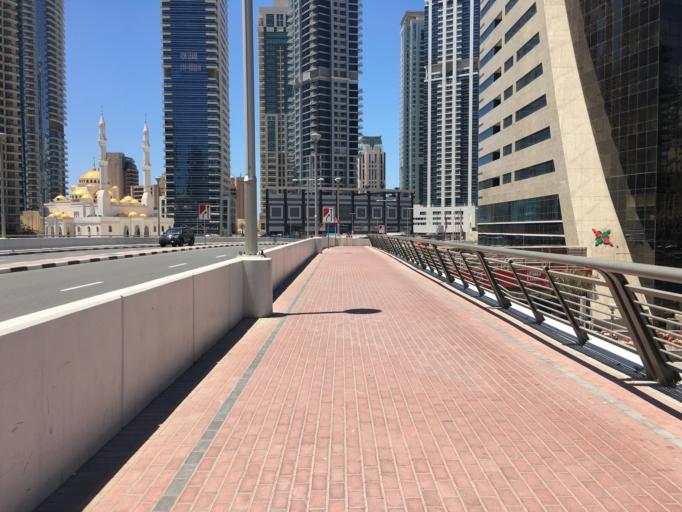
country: AE
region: Dubai
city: Dubai
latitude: 25.0826
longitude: 55.1444
